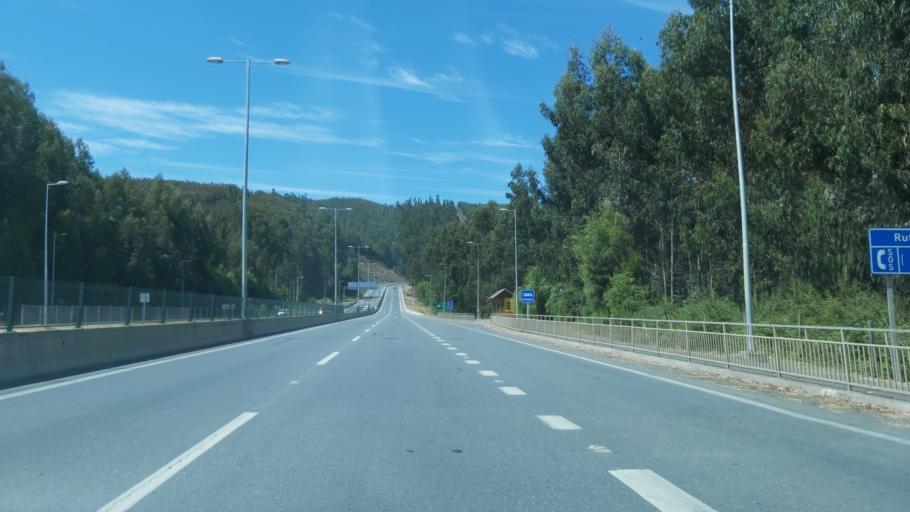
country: CL
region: Biobio
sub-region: Provincia de Concepcion
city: Lota
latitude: -37.1134
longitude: -73.1486
